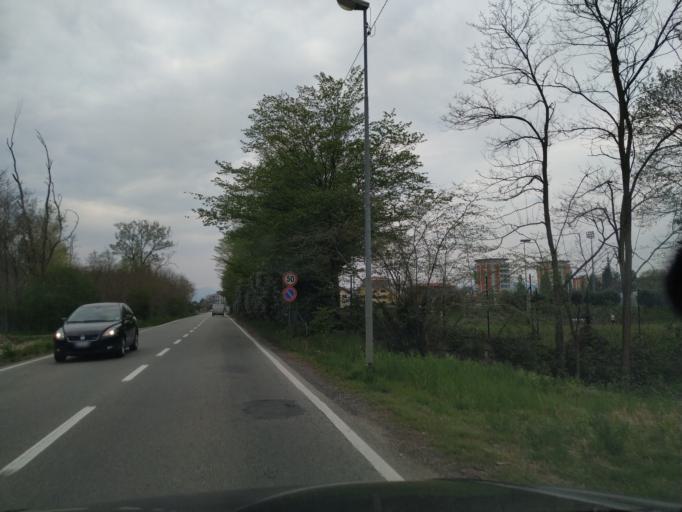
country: IT
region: Piedmont
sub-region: Provincia di Novara
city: Borgomanero
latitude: 45.6912
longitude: 8.4555
